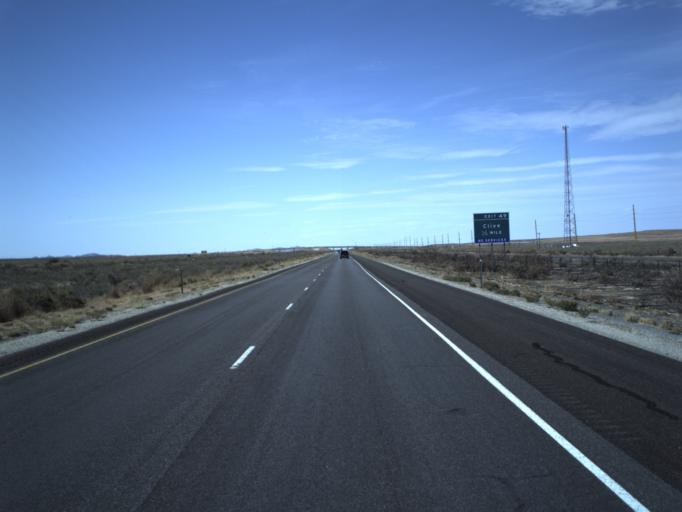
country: US
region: Utah
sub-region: Tooele County
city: Grantsville
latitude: 40.7373
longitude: -113.0960
